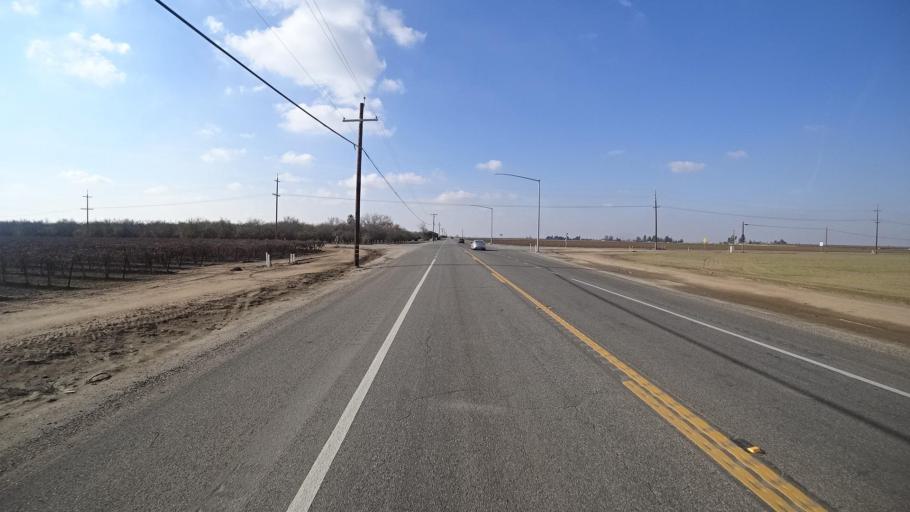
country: US
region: California
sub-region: Kern County
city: Weedpatch
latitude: 35.2088
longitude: -118.8773
